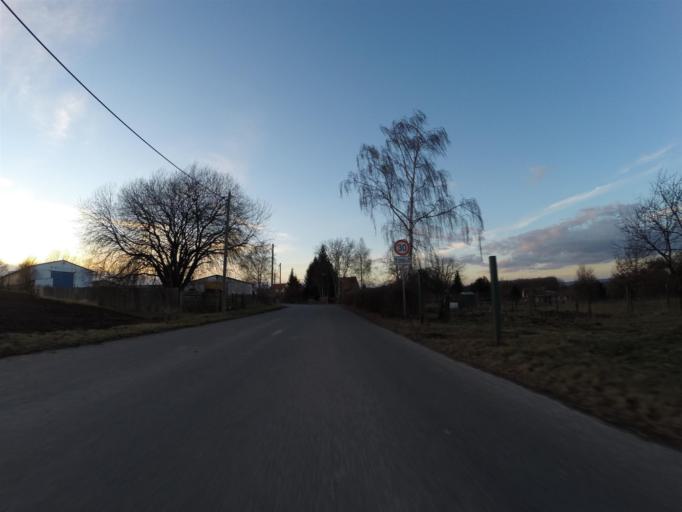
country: DE
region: Thuringia
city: Apolda
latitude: 50.9994
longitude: 11.5248
